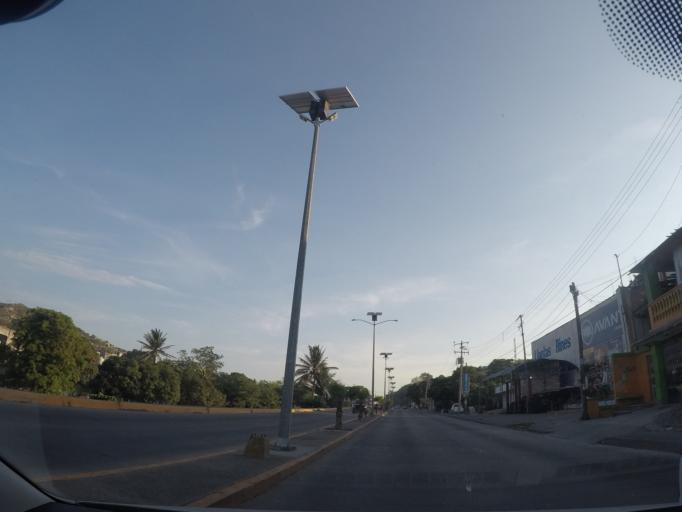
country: MX
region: Oaxaca
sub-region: Salina Cruz
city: Salina Cruz
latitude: 16.1911
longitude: -95.2017
